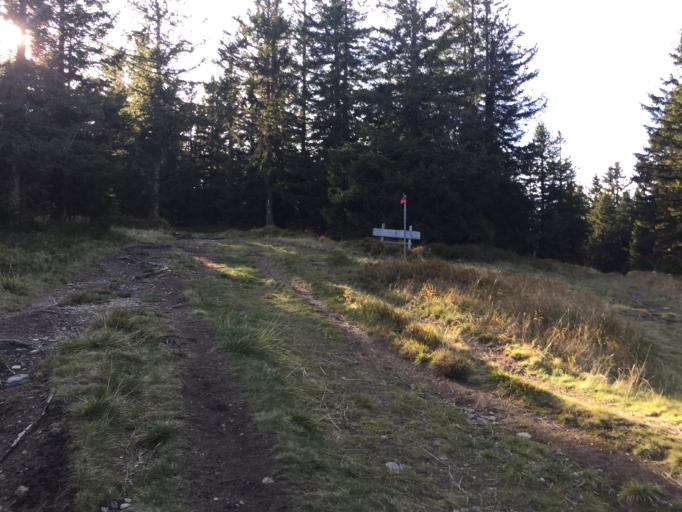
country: SI
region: Mislinja
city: Mislinja
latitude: 46.4879
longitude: 15.2382
